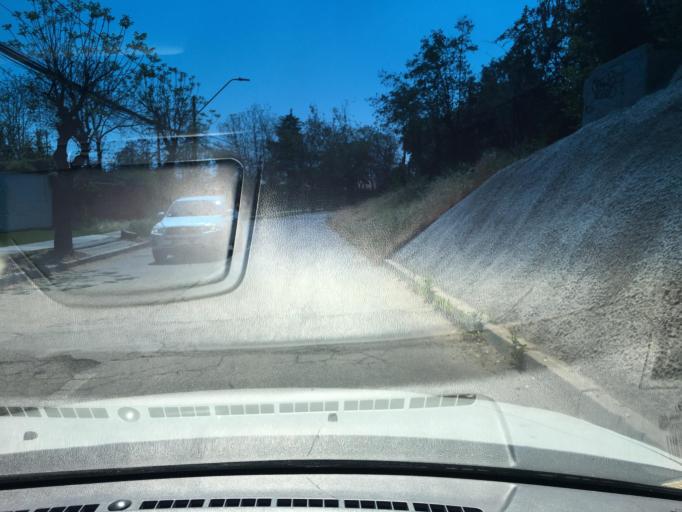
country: CL
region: Santiago Metropolitan
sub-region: Provincia de Santiago
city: Villa Presidente Frei, Nunoa, Santiago, Chile
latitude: -33.5257
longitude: -70.5695
